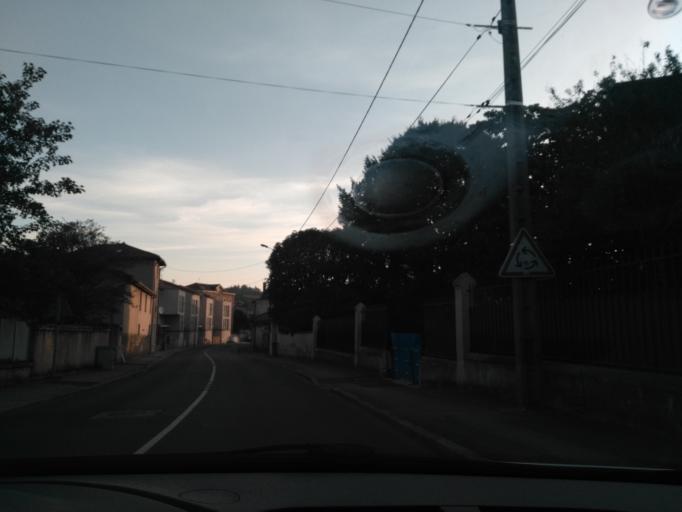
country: FR
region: Rhone-Alpes
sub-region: Departement du Rhone
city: Albigny-sur-Saone
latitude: 45.8758
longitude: 4.8337
